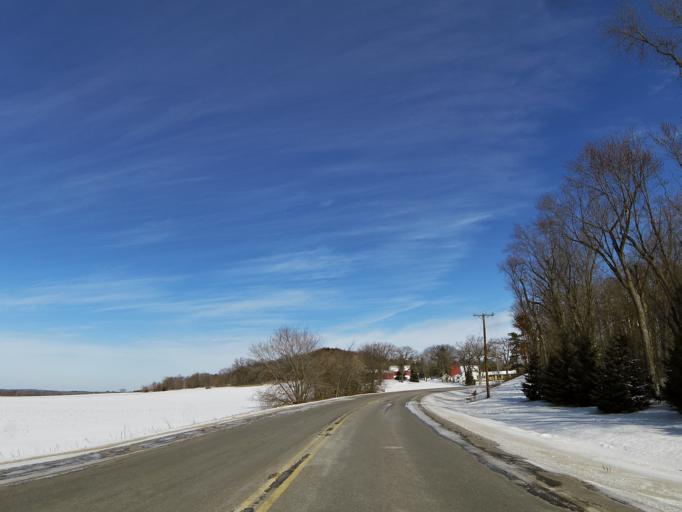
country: US
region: Wisconsin
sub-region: Pierce County
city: Prescott
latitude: 44.8053
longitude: -92.7511
